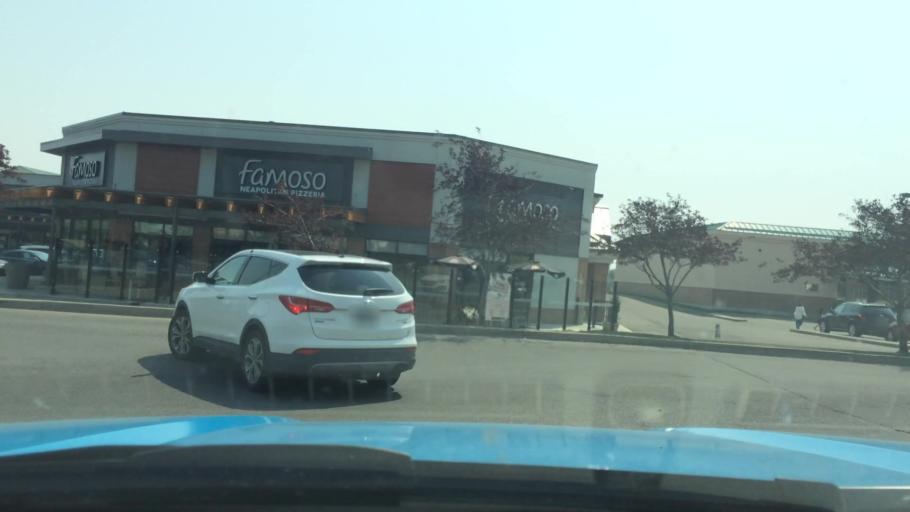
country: CA
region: Alberta
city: Calgary
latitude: 51.1381
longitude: -114.1599
